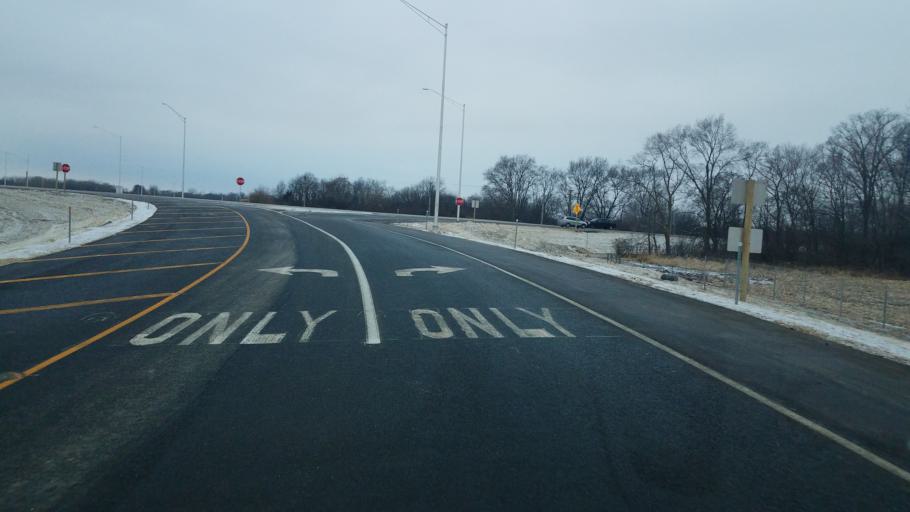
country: US
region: Illinois
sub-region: Kane County
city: Sugar Grove
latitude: 41.8201
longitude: -88.4655
